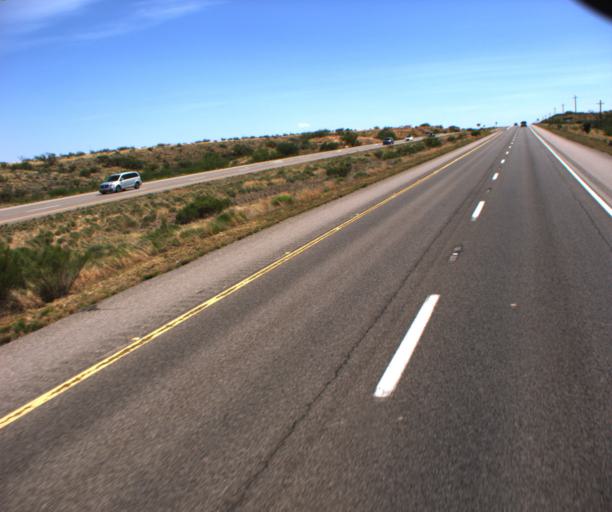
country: US
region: Arizona
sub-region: Cochise County
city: Whetstone
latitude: 31.9302
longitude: -110.3413
